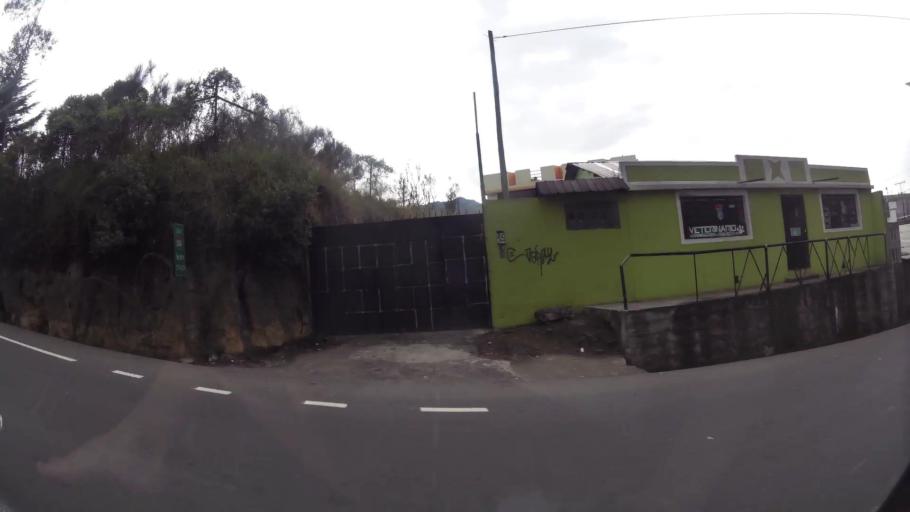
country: EC
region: Pichincha
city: Sangolqui
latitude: -0.3666
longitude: -78.5509
